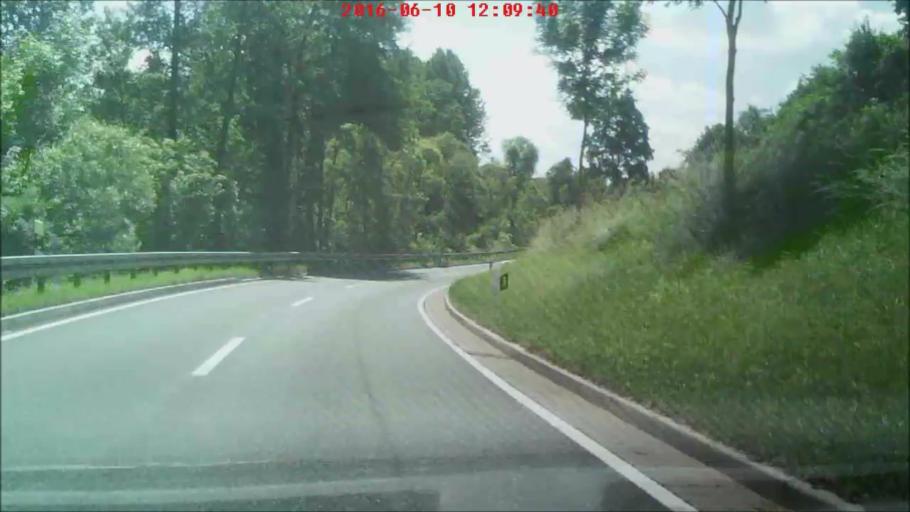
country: DE
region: Thuringia
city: Ellingshausen
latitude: 50.5514
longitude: 10.4742
